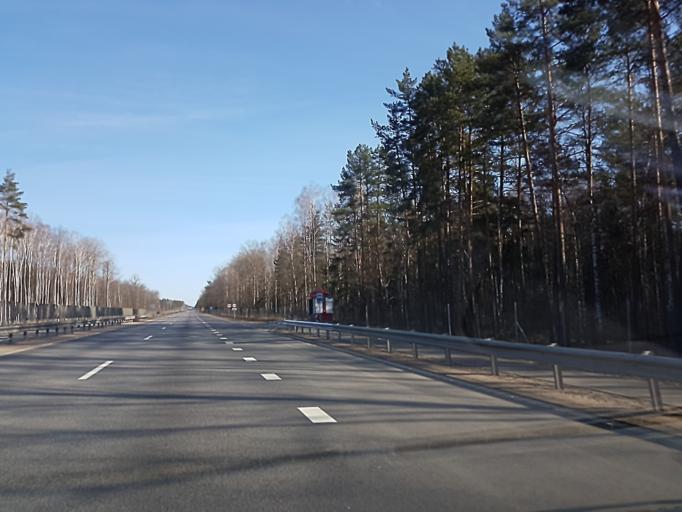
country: BY
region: Mogilev
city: Asipovichy
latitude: 53.3744
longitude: 28.5762
